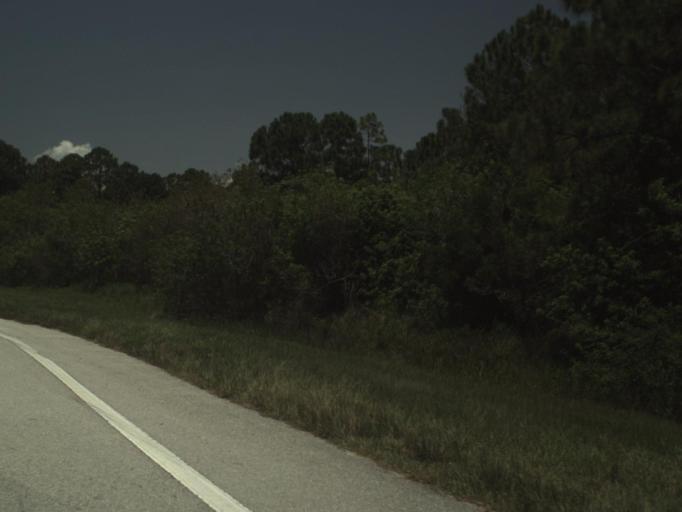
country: US
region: Florida
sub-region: Martin County
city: Palm City
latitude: 27.1620
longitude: -80.3822
